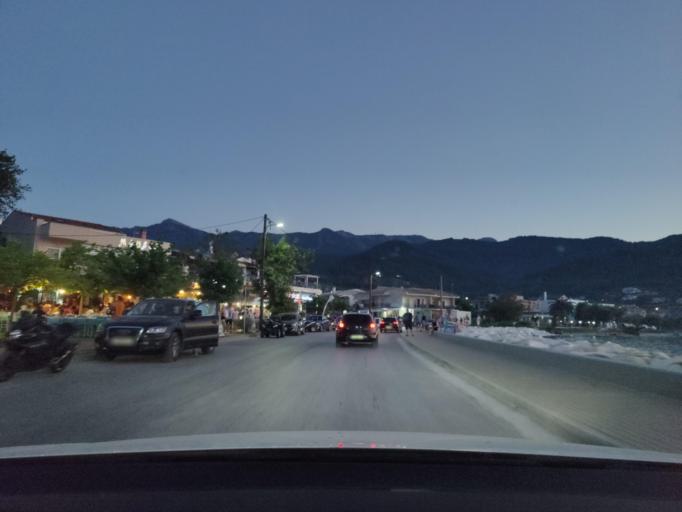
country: GR
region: East Macedonia and Thrace
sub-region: Nomos Kavalas
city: Thasos
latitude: 40.7778
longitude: 24.7006
